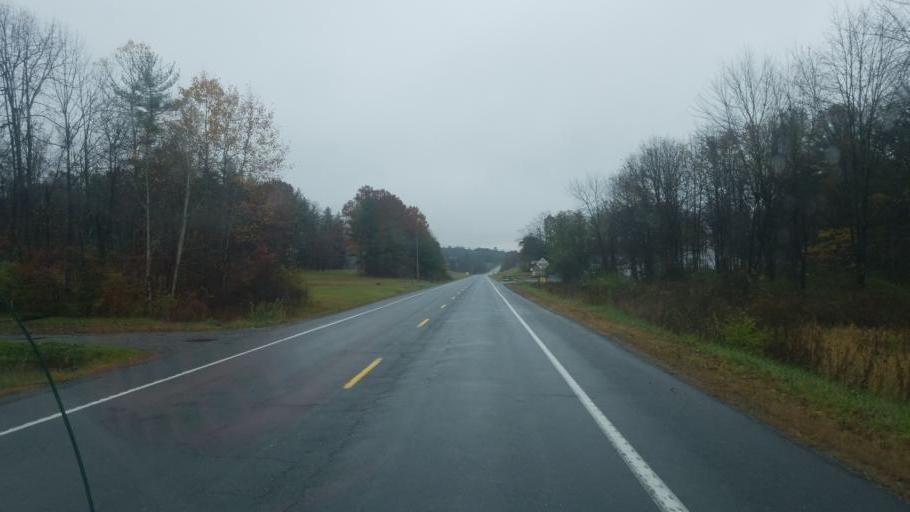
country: US
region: Pennsylvania
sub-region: Centre County
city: Milesburg
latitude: 40.9864
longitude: -77.7202
